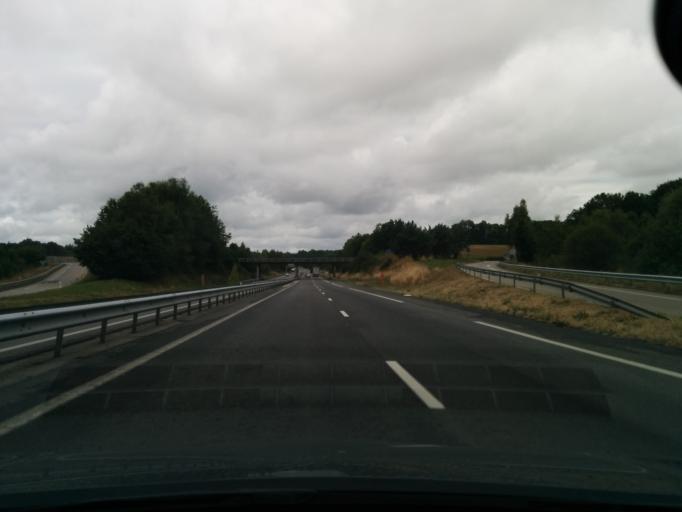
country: FR
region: Limousin
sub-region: Departement de la Haute-Vienne
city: Saint-Germain-les-Belles
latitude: 45.5832
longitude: 1.4753
